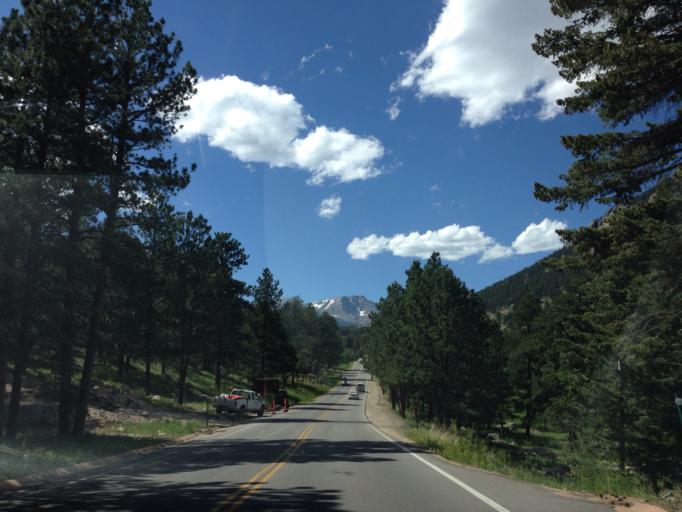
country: US
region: Colorado
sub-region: Larimer County
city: Estes Park
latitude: 40.3629
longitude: -105.5824
